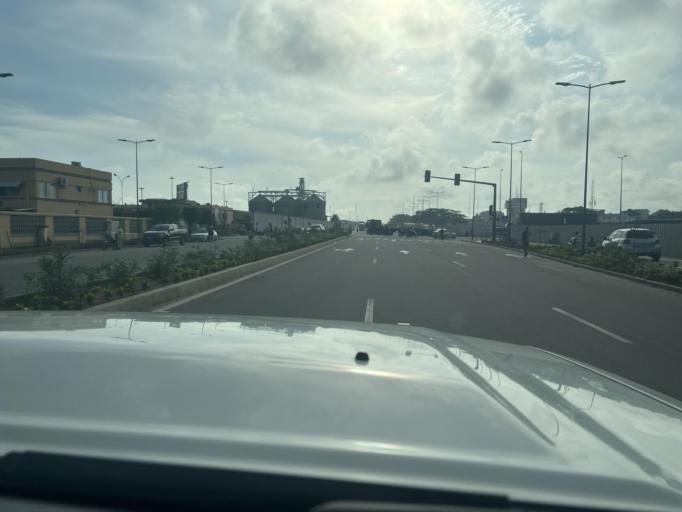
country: BJ
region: Littoral
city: Cotonou
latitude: 6.3512
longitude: 2.4287
